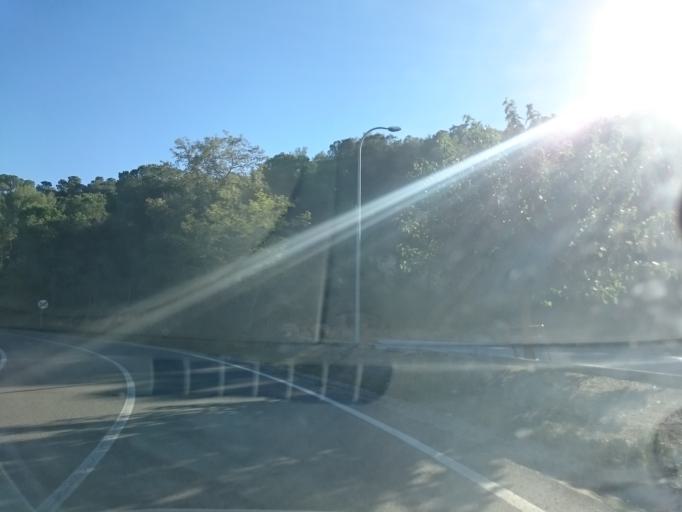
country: ES
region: Catalonia
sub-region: Provincia de Barcelona
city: Capellades
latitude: 41.5363
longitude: 1.6795
